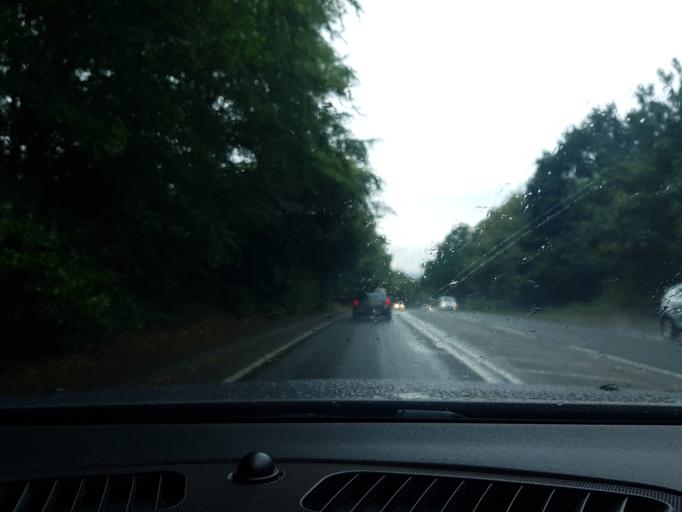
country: GB
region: England
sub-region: Surrey
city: Farnham
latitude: 51.2373
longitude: -0.8322
